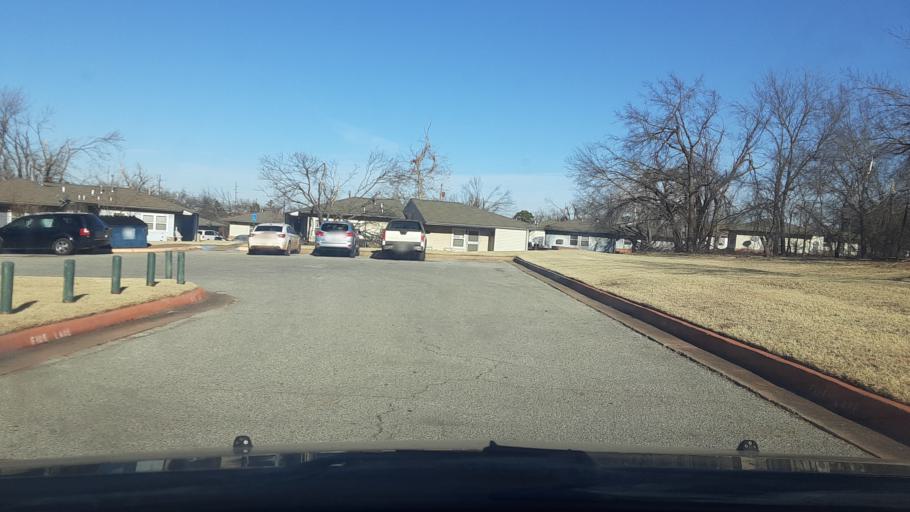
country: US
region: Oklahoma
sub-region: Logan County
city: Guthrie
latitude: 35.8759
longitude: -97.4048
